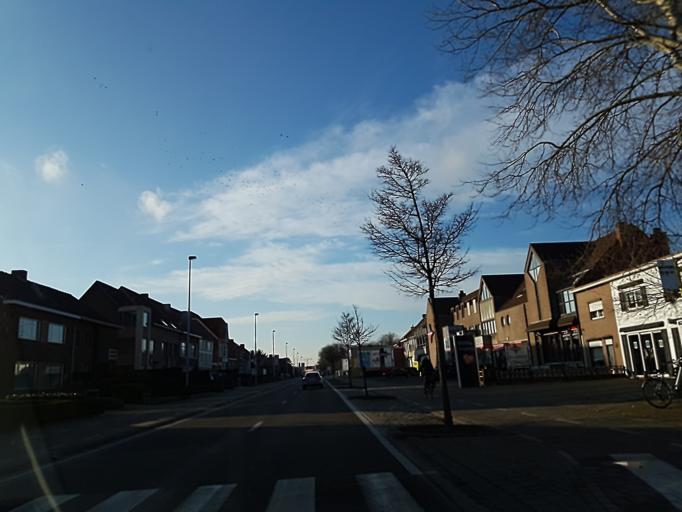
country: BE
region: Flanders
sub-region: Provincie Antwerpen
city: Oud-Turnhout
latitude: 51.3202
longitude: 4.9749
